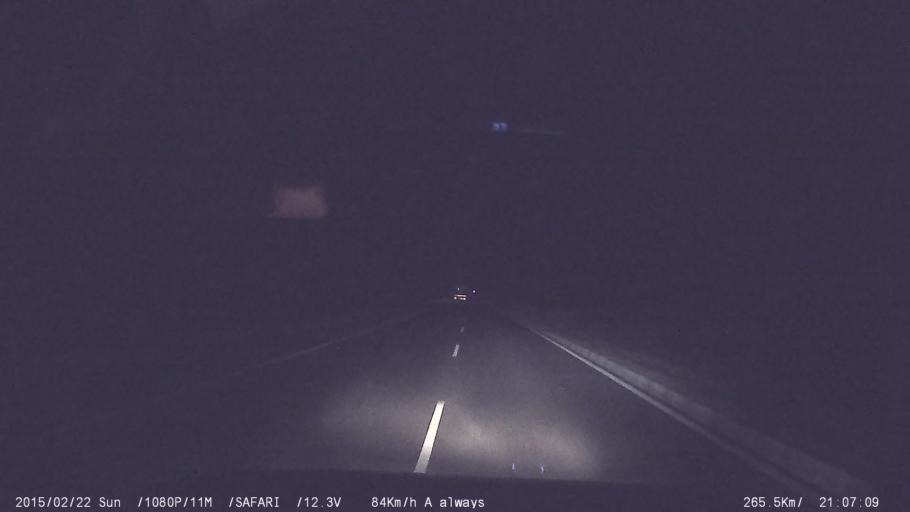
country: IN
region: Tamil Nadu
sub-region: Karur
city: Pallappatti
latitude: 10.7186
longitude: 77.9288
